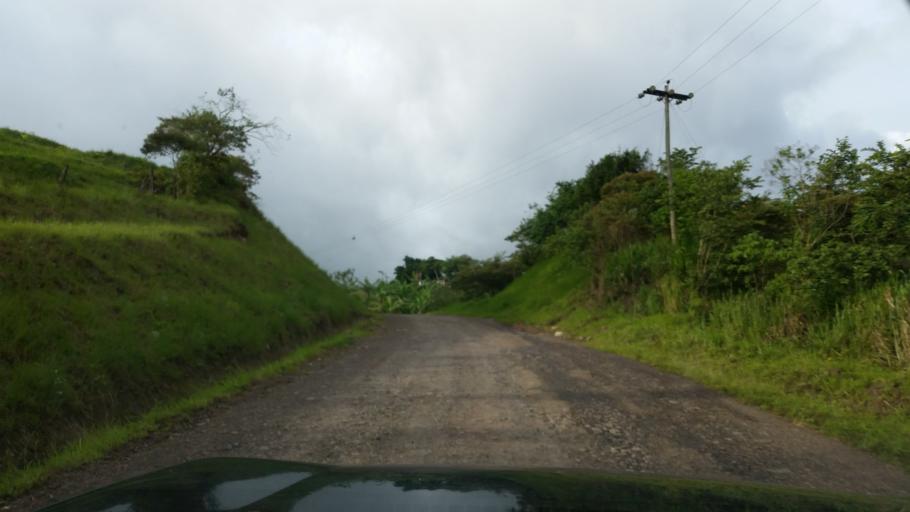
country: NI
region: Jinotega
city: Jinotega
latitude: 13.2663
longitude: -85.7303
